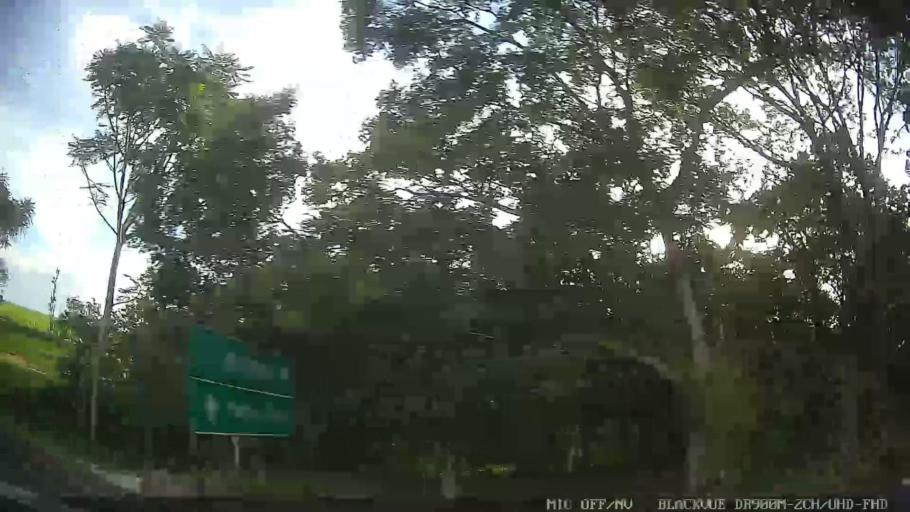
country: BR
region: Sao Paulo
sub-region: Tiete
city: Tiete
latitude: -23.1435
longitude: -47.6725
